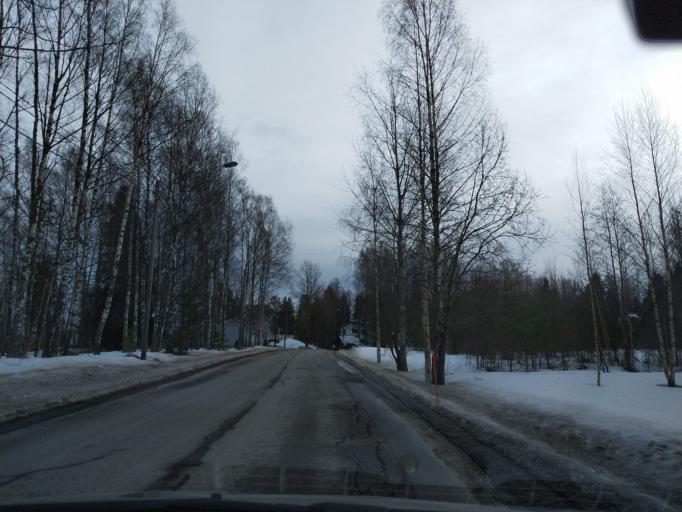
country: FI
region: Uusimaa
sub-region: Helsinki
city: Sibbo
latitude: 60.2654
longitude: 25.2868
